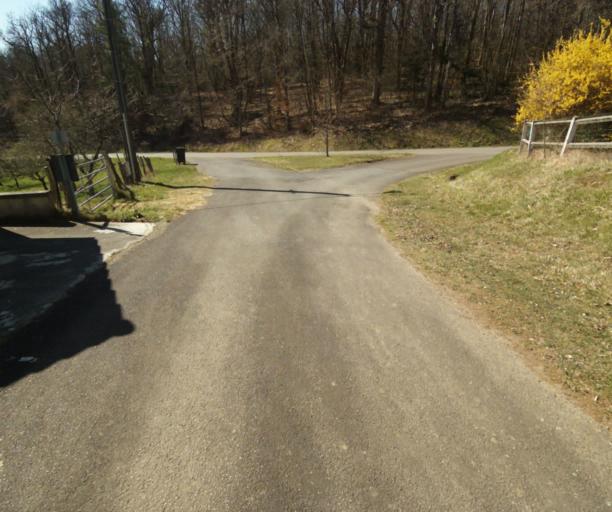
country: FR
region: Limousin
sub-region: Departement de la Correze
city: Saint-Clement
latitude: 45.3454
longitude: 1.6400
